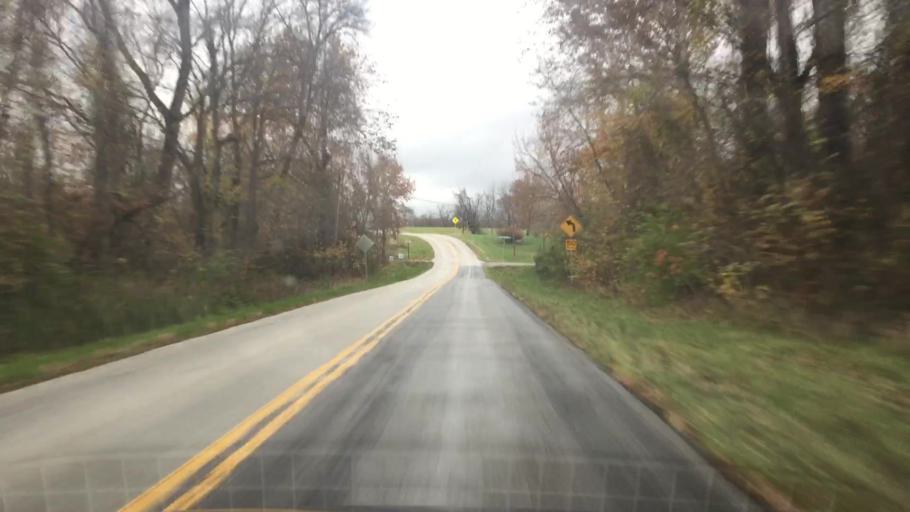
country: US
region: Missouri
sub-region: Boone County
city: Columbia
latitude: 38.9138
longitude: -92.4695
